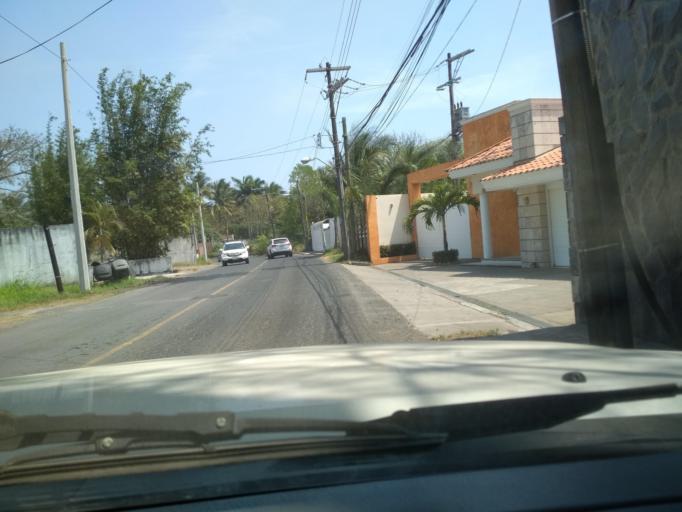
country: MX
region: Veracruz
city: Boca del Rio
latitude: 19.0960
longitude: -96.1270
